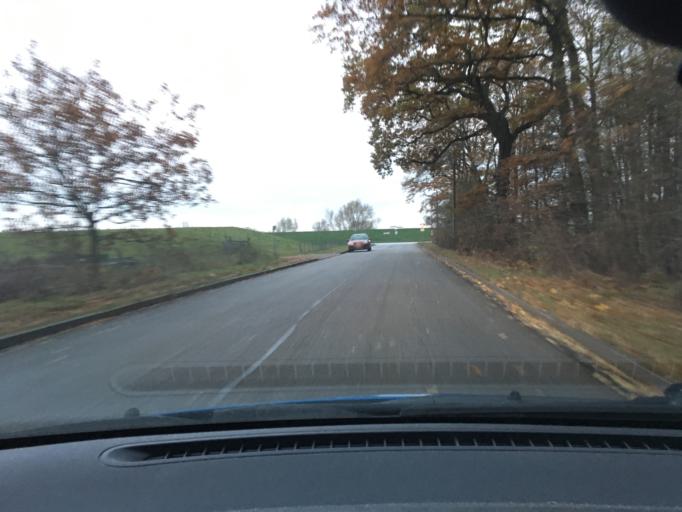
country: DE
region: Lower Saxony
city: Winsen
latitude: 53.4031
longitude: 10.2058
